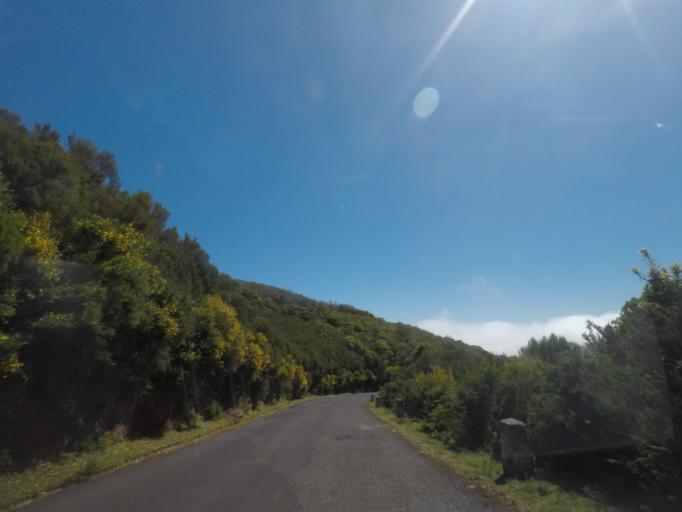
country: PT
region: Madeira
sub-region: Calheta
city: Estreito da Calheta
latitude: 32.7857
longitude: -17.1826
